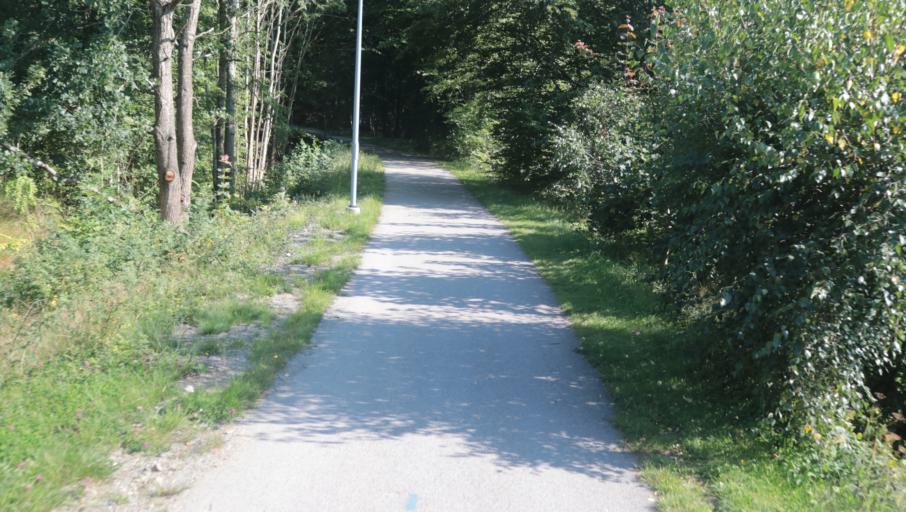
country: SE
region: Blekinge
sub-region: Karlshamns Kommun
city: Svangsta
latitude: 56.2568
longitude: 14.7753
